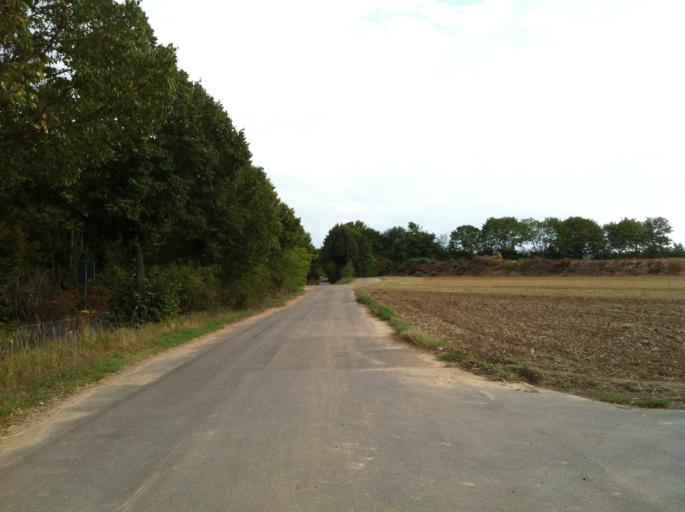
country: DE
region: Rheinland-Pfalz
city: Mainz
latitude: 49.9864
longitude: 8.2301
